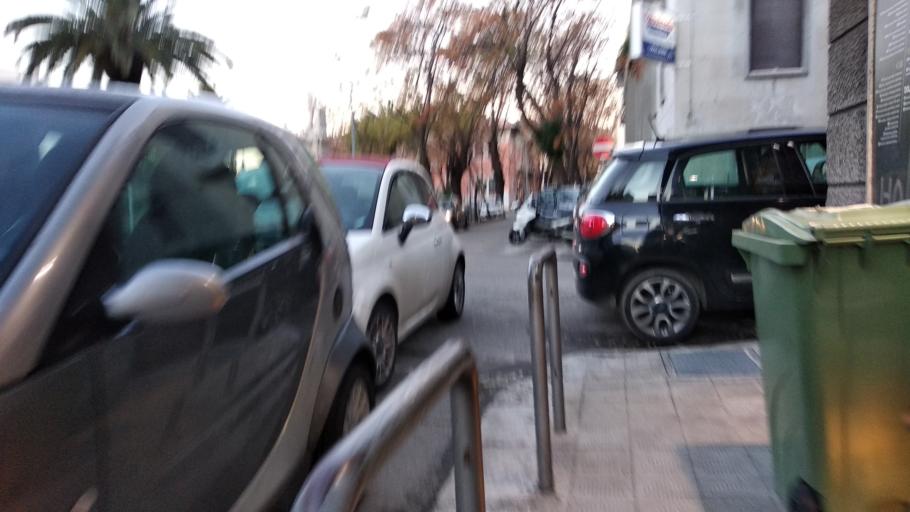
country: IT
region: Calabria
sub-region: Provincia di Reggio Calabria
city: Reggio Calabria
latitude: 38.1138
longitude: 15.6513
